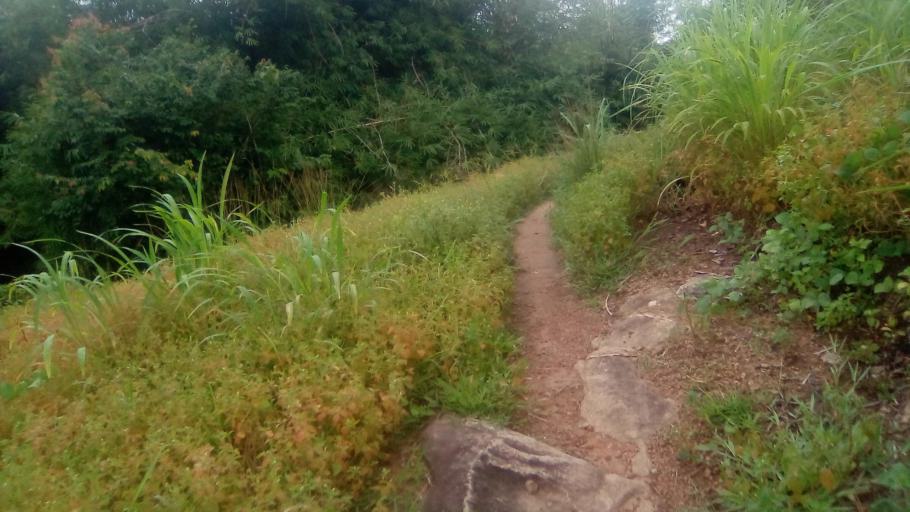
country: SL
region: Southern Province
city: Moyamba
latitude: 8.1547
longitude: -12.4251
